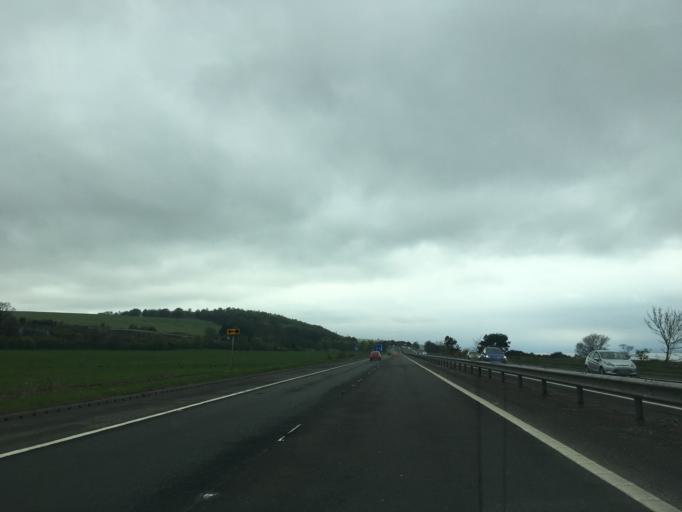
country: GB
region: Scotland
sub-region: West Dunbartonshire
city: Dumbarton
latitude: 55.9230
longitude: -4.5419
